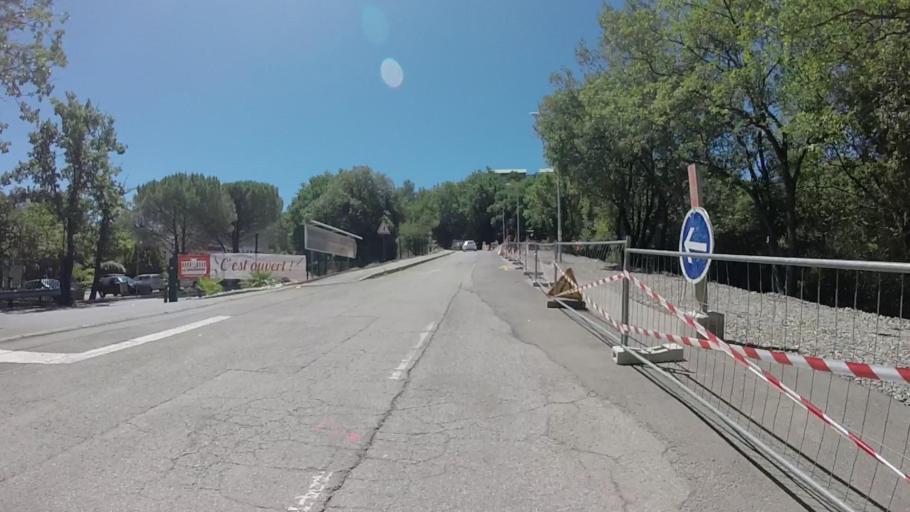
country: FR
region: Provence-Alpes-Cote d'Azur
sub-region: Departement des Alpes-Maritimes
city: Biot
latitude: 43.6203
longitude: 7.0557
